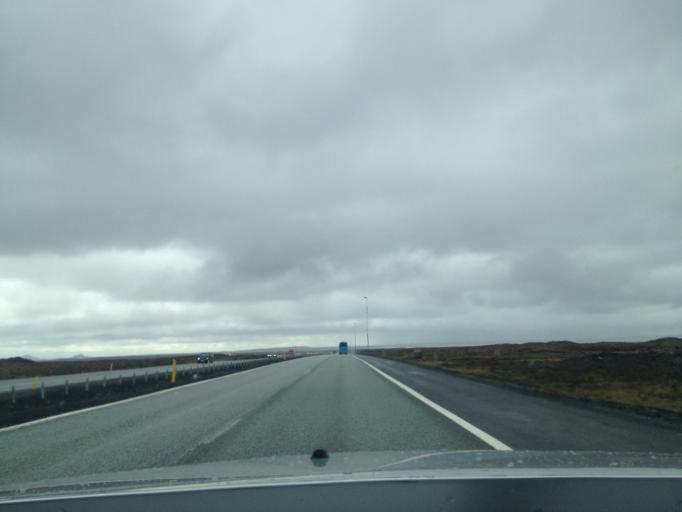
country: IS
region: Southern Peninsula
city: Vogar
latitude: 63.9999
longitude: -22.2460
